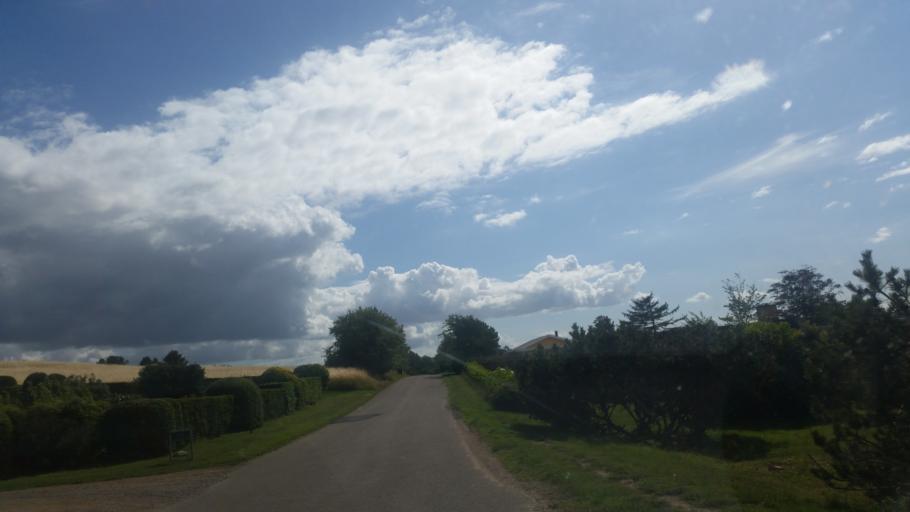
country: DK
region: Zealand
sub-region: Odsherred Kommune
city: Horve
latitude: 55.8167
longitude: 11.4144
